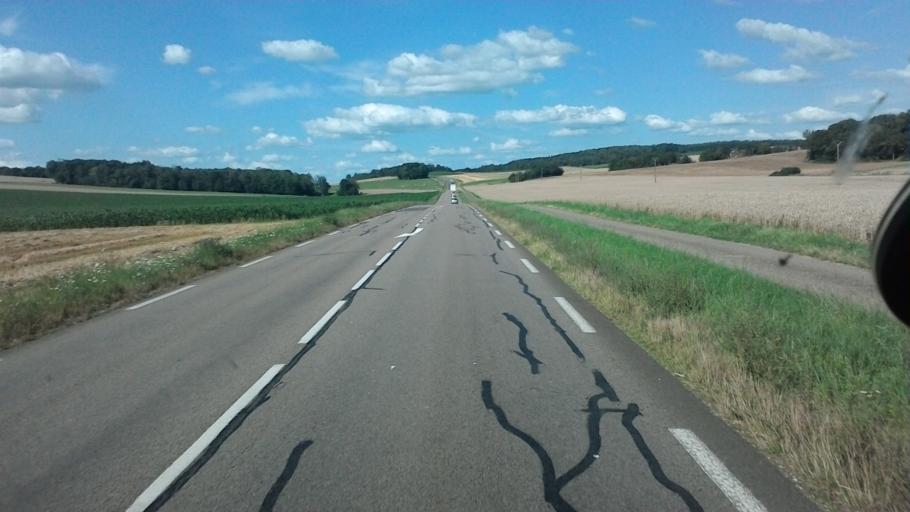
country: FR
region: Franche-Comte
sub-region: Departement de la Haute-Saone
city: Echenoz-la-Meline
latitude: 47.5446
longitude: 6.0545
